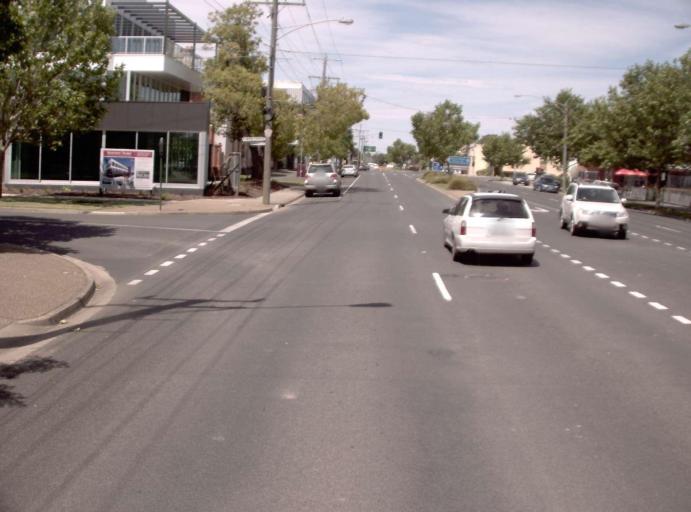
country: AU
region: Victoria
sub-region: Wellington
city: Sale
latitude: -38.1115
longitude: 147.0640
